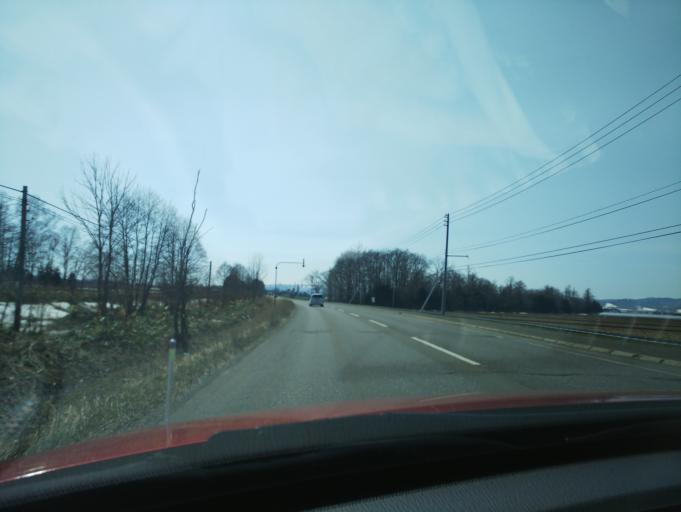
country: JP
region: Hokkaido
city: Nayoro
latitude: 44.3052
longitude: 142.4361
